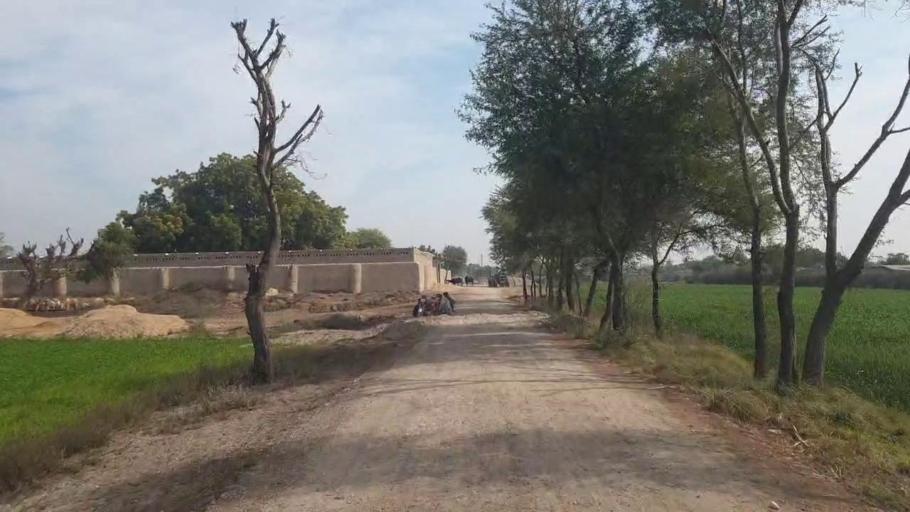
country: PK
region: Sindh
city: Nawabshah
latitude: 26.1279
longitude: 68.4948
